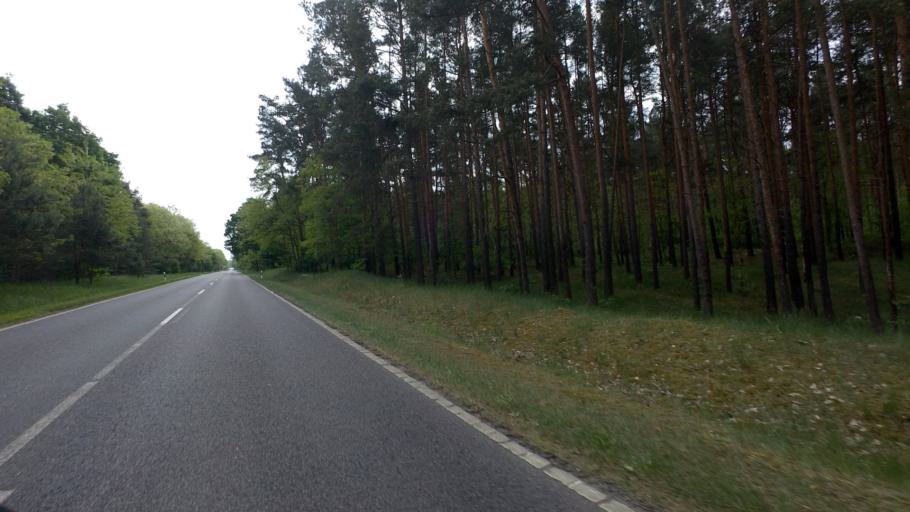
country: DE
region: Brandenburg
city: Lieberose
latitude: 51.9650
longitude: 14.3165
